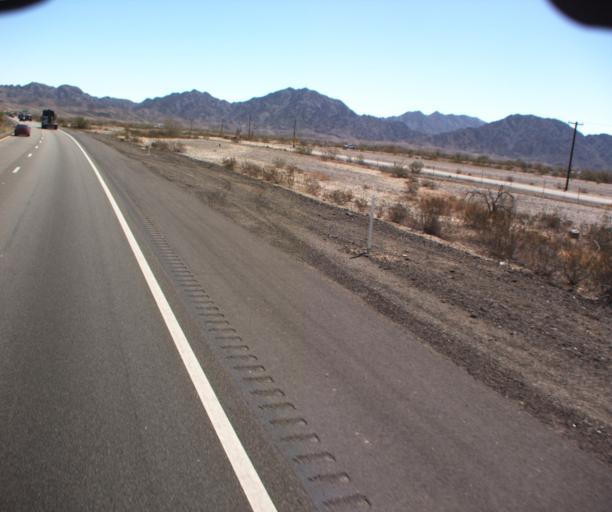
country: US
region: Arizona
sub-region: Yuma County
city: Fortuna Foothills
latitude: 32.6612
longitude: -114.3778
